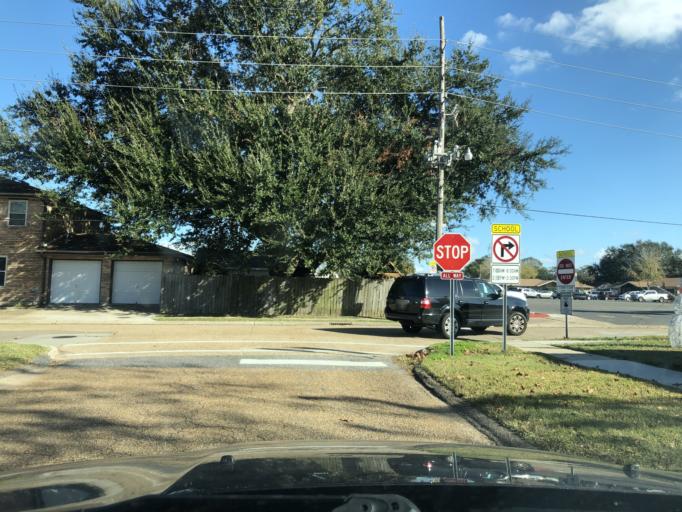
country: US
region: Louisiana
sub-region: Jefferson Parish
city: Metairie Terrace
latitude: 29.9902
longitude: -90.1648
